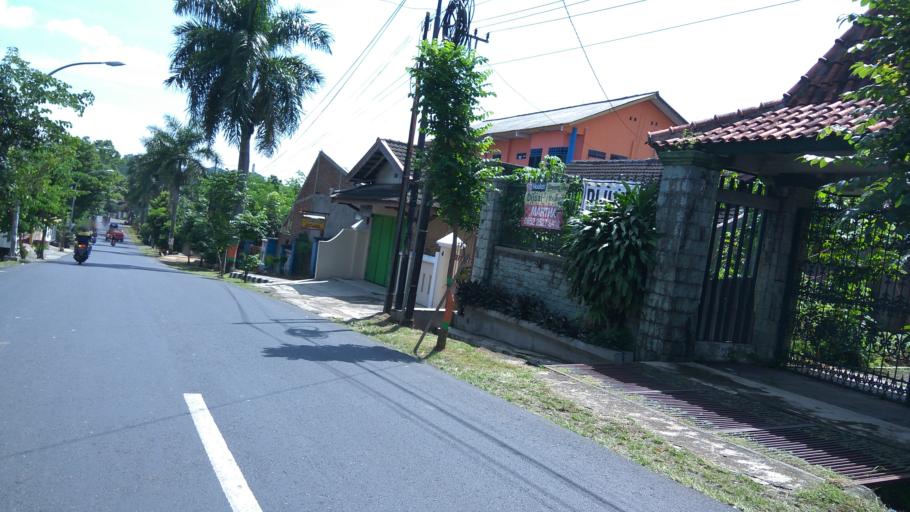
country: ID
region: Central Java
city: Ungaran
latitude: -7.1193
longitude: 110.4042
